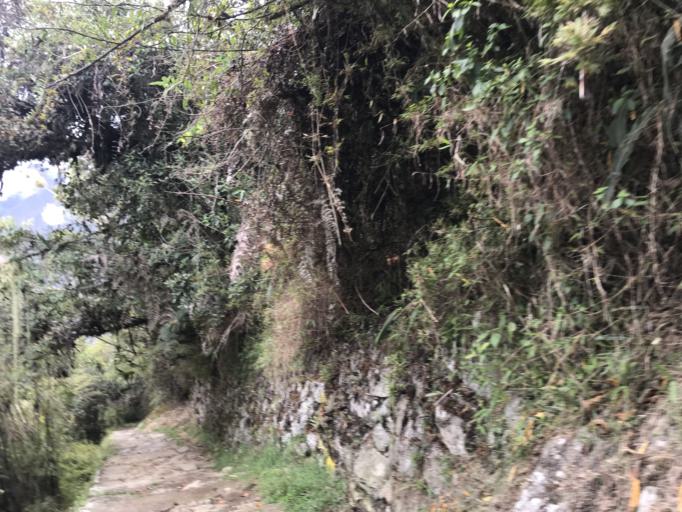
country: PE
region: Cusco
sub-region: Provincia de La Convencion
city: Santa Teresa
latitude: -13.1698
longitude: -72.5339
